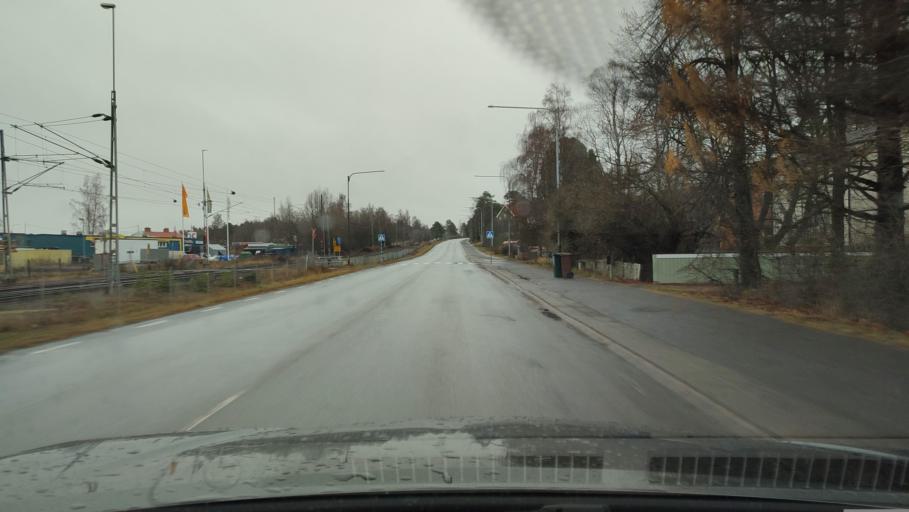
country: SE
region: Vaesterbotten
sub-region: Umea Kommun
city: Holmsund
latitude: 63.7093
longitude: 20.3717
